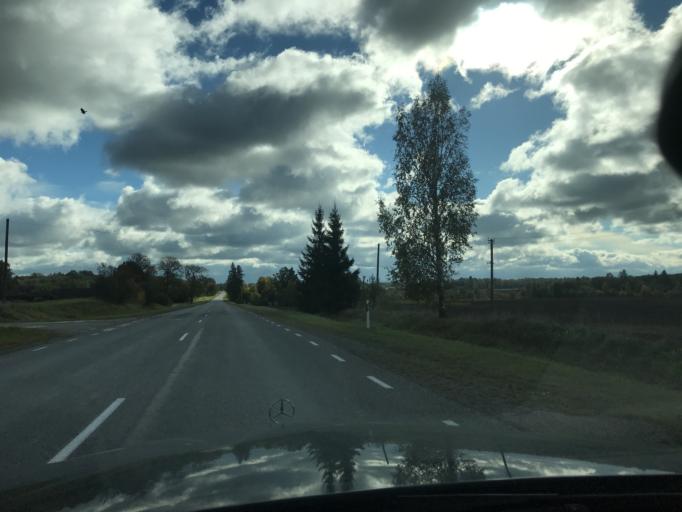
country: EE
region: Vorumaa
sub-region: Antsla vald
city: Vana-Antsla
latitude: 57.9499
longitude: 26.2887
